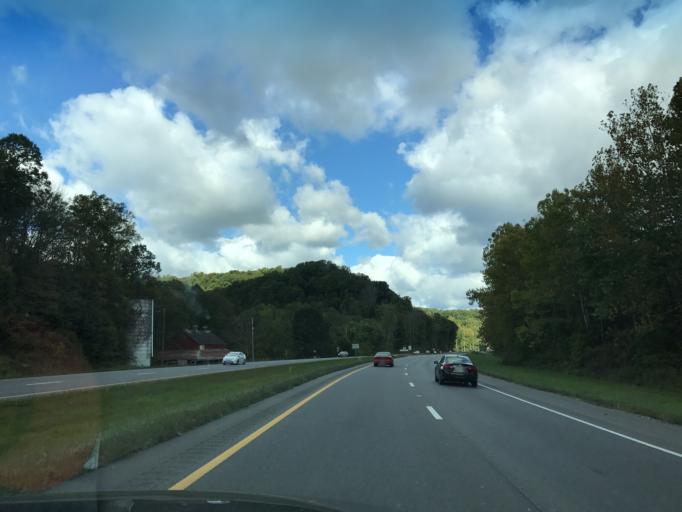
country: US
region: Ohio
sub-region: Fairfield County
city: Geneva
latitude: 39.5908
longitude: -82.5426
